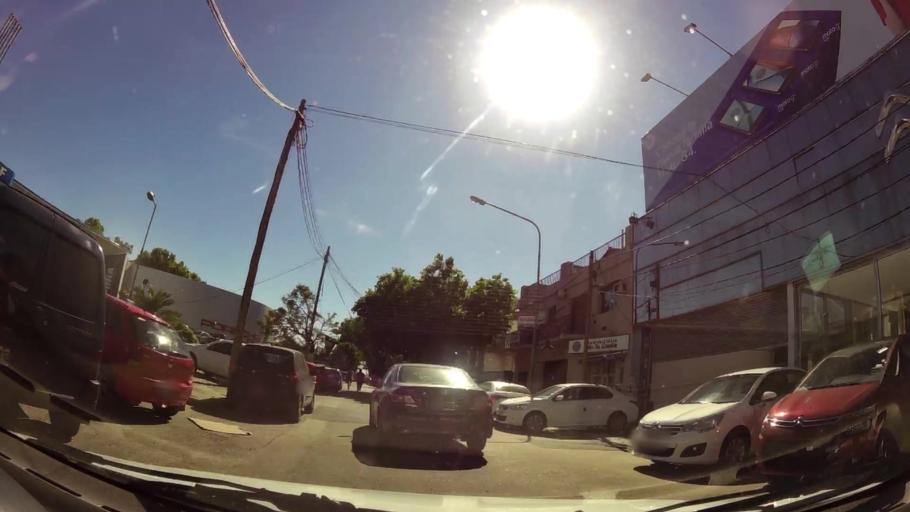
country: AR
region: Buenos Aires
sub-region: Partido de Vicente Lopez
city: Olivos
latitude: -34.5257
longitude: -58.4715
